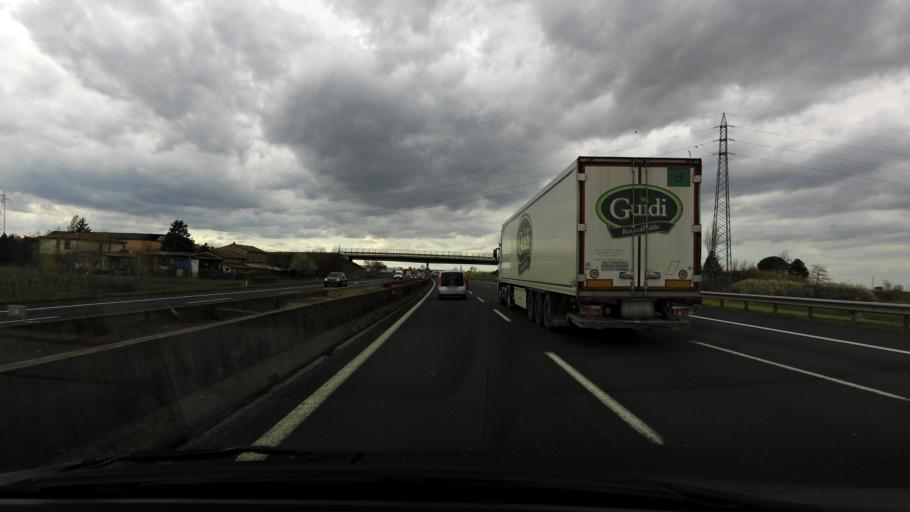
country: IT
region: Emilia-Romagna
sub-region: Forli-Cesena
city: Forli
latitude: 44.2594
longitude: 12.0721
